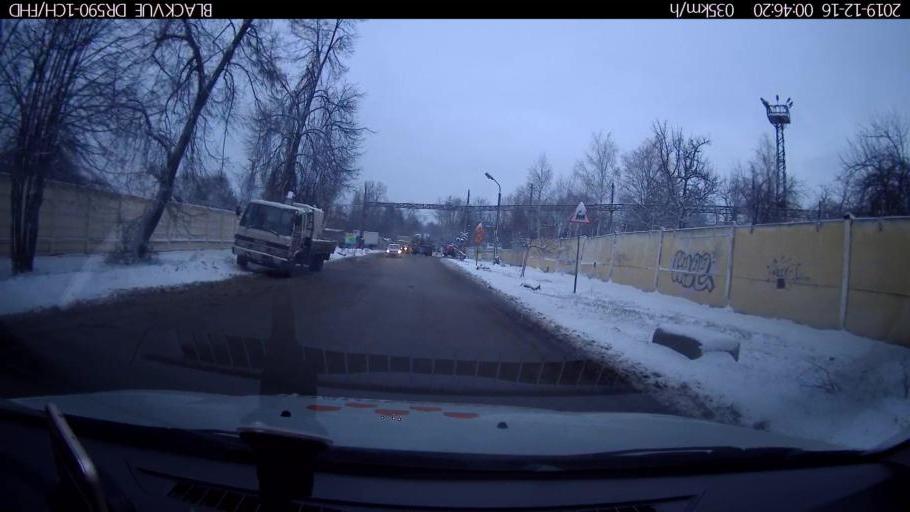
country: RU
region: Nizjnij Novgorod
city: Gorbatovka
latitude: 56.3103
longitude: 43.8584
